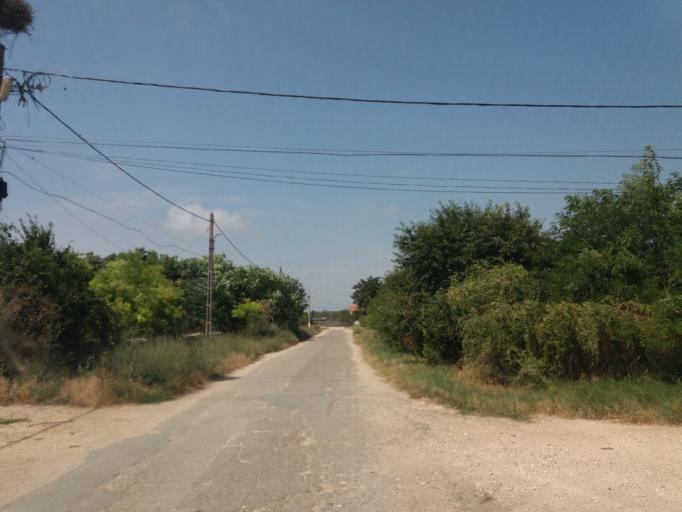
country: RO
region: Constanta
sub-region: Comuna Sacele
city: Sacele
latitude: 44.4571
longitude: 28.7367
